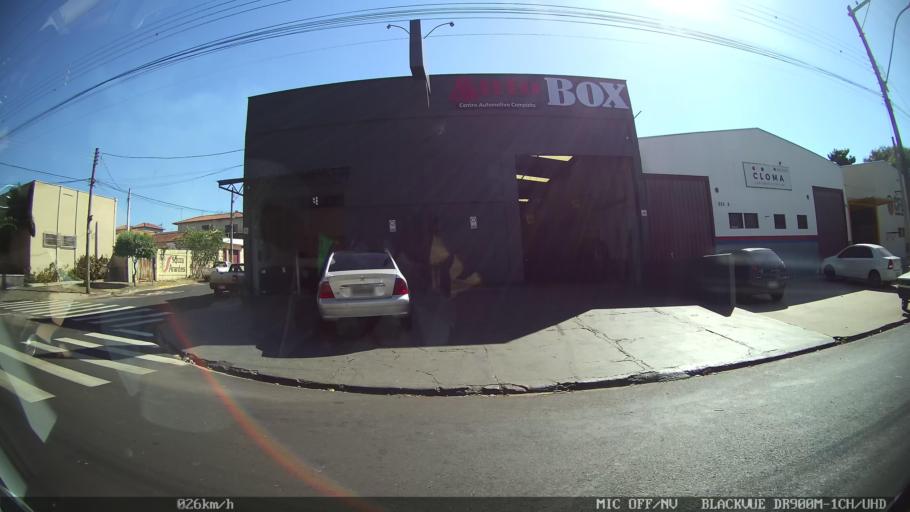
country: BR
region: Sao Paulo
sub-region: Batatais
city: Batatais
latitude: -20.8825
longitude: -47.5943
